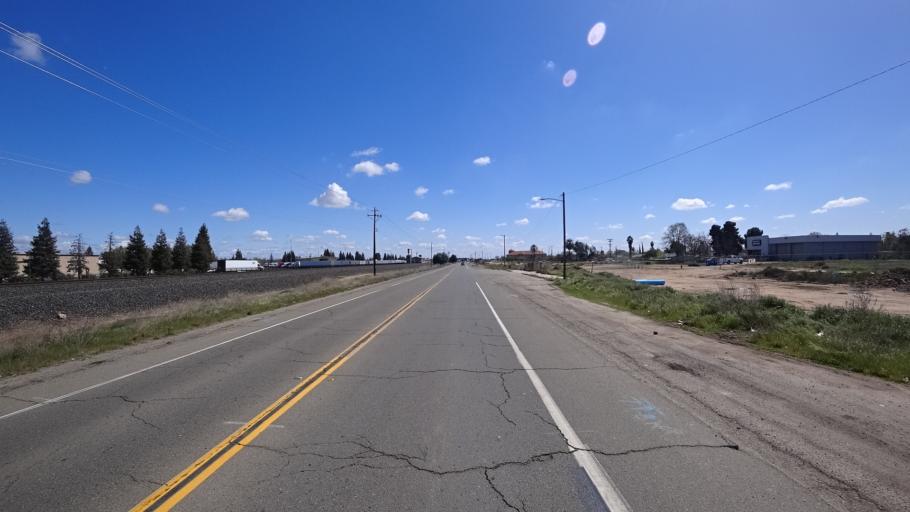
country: US
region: California
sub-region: Fresno County
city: West Park
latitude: 36.8136
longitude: -119.8851
